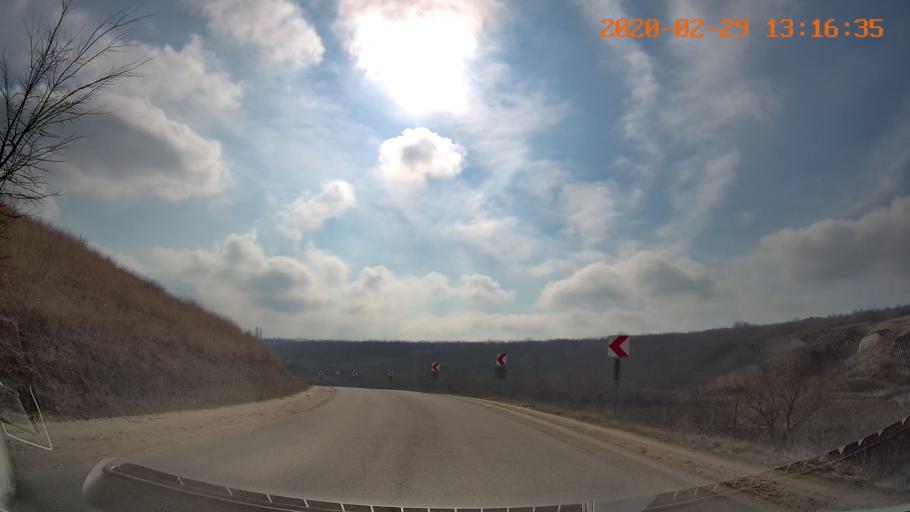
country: MD
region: Telenesti
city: Camenca
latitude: 48.0015
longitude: 28.6628
